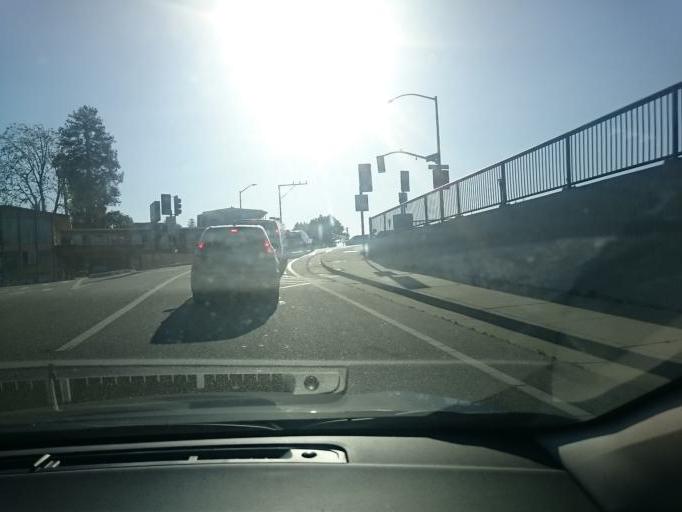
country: US
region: California
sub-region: Santa Cruz County
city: Santa Cruz
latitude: 36.9676
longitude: -122.0183
